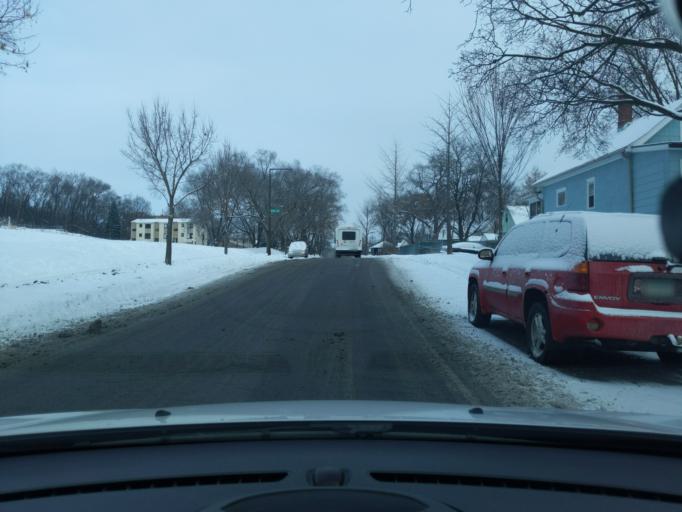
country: US
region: Minnesota
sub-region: Ramsey County
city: Falcon Heights
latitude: 44.9608
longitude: -93.1365
